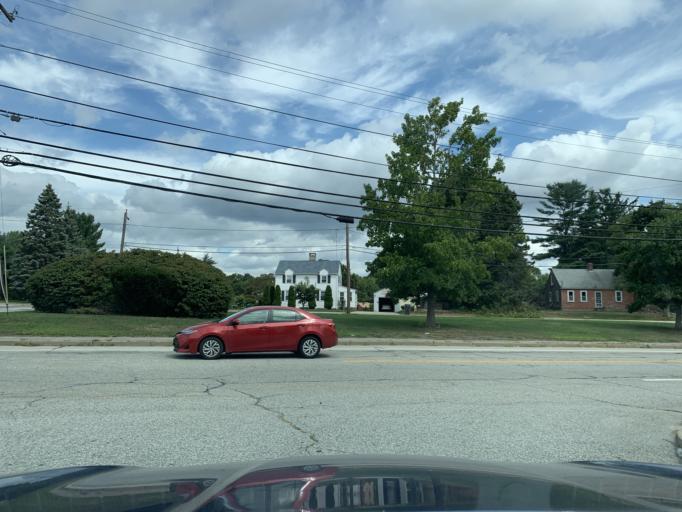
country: US
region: Rhode Island
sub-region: Providence County
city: Johnston
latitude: 41.7810
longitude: -71.4948
